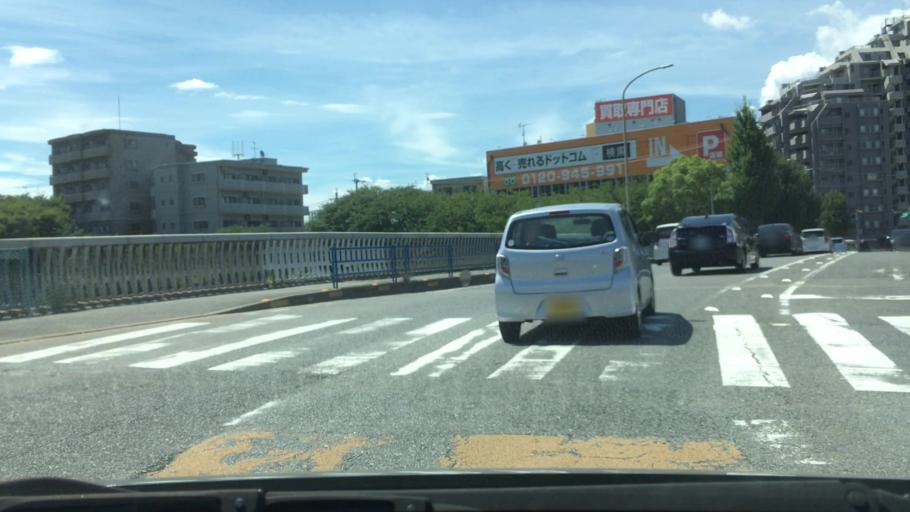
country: JP
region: Fukuoka
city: Fukuoka-shi
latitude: 33.5748
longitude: 130.4219
